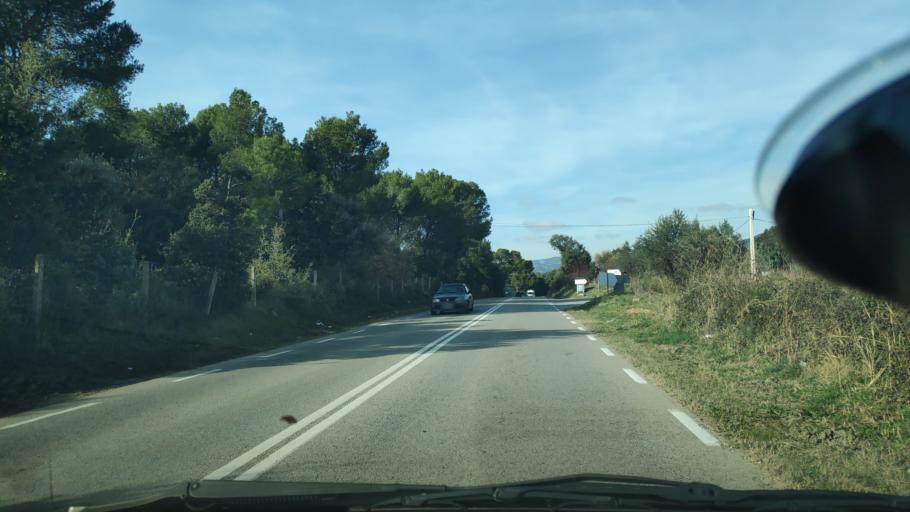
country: ES
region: Catalonia
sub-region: Provincia de Barcelona
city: Matadepera
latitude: 41.5914
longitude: 2.0435
